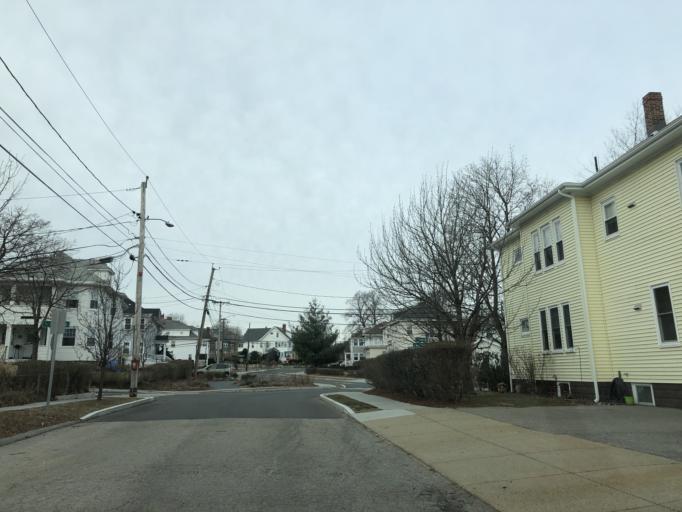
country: US
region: Massachusetts
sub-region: Middlesex County
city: Watertown
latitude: 42.3675
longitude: -71.1646
